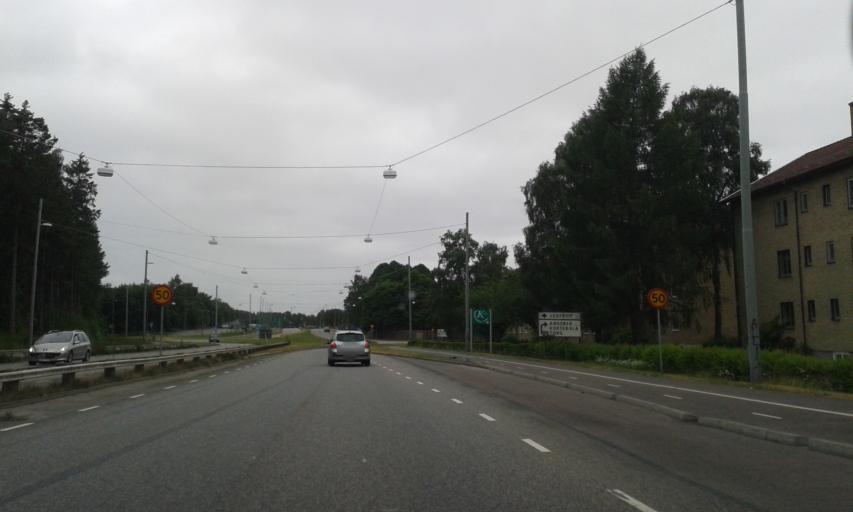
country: SE
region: Vaestra Goetaland
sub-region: Goteborg
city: Eriksbo
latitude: 57.7513
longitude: 12.0373
